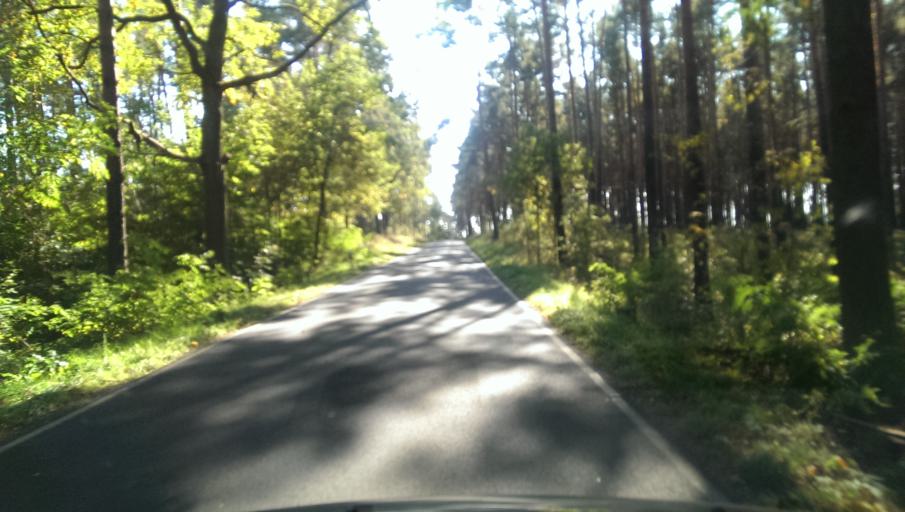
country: DE
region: Brandenburg
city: Halbe
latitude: 52.0654
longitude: 13.7227
